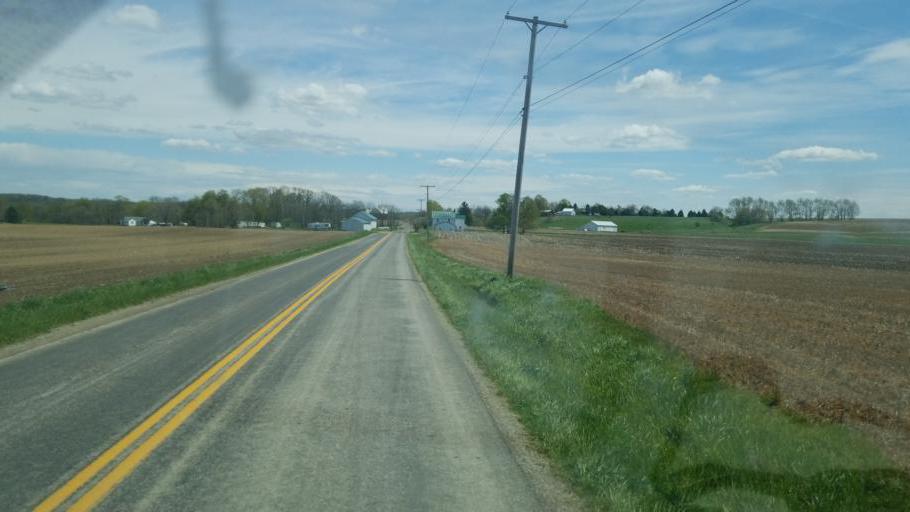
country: US
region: Ohio
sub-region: Ashland County
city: Loudonville
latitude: 40.7581
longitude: -82.1518
